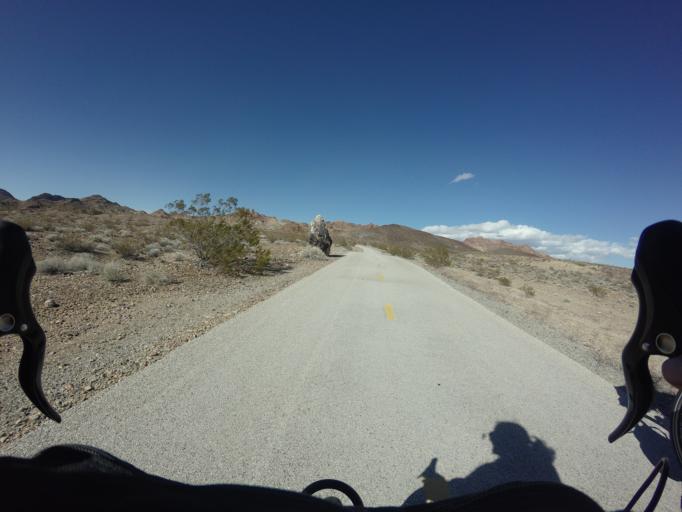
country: US
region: Nevada
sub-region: Clark County
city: Boulder City
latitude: 35.9704
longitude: -114.8759
